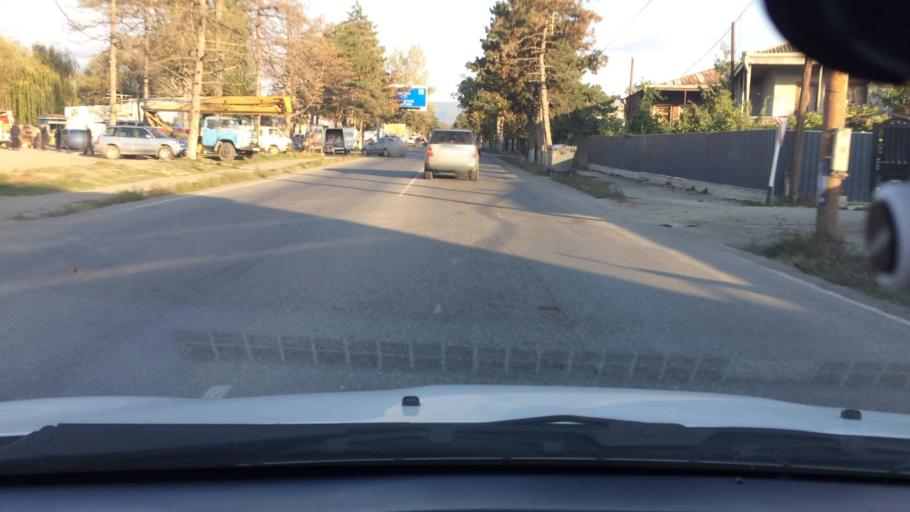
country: GE
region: Shida Kartli
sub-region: Khashuris Raioni
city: Khashuri
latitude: 41.9882
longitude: 43.5926
